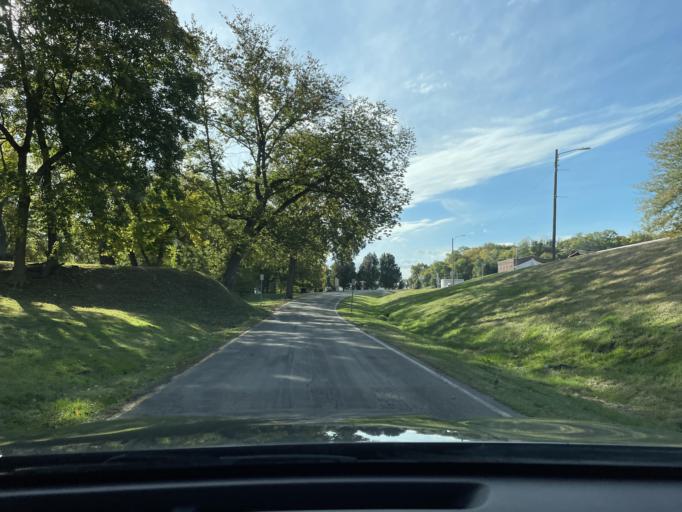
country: US
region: Kansas
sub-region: Doniphan County
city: Elwood
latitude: 39.7114
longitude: -94.8541
